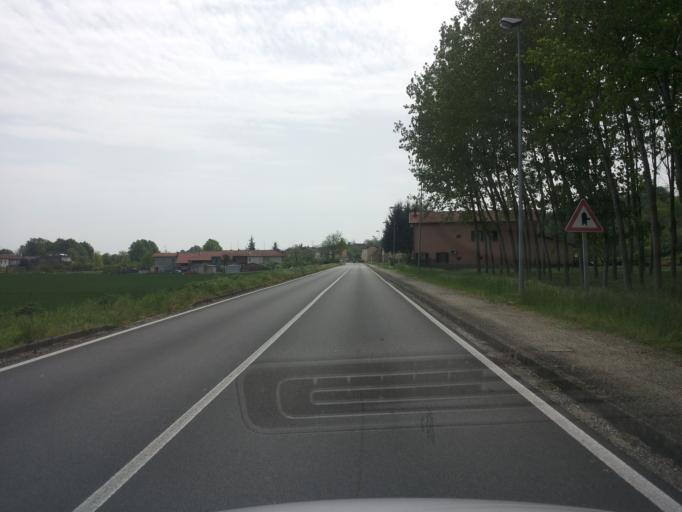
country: IT
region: Piedmont
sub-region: Provincia di Alessandria
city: Terruggia
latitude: 45.0922
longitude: 8.4621
